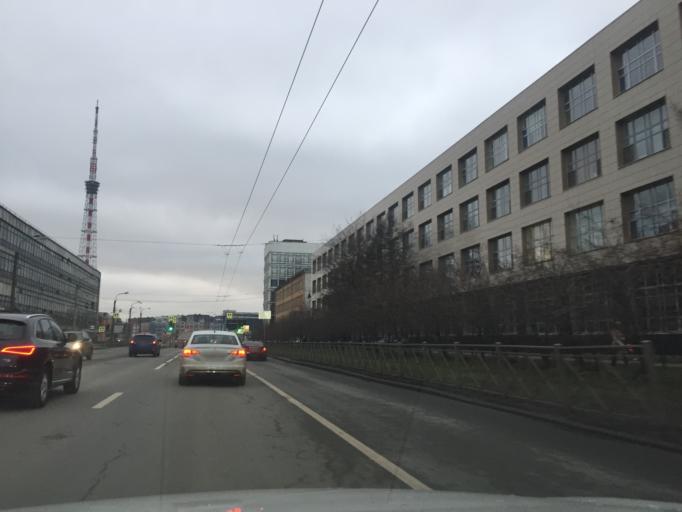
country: RU
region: Leningrad
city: Sampsonievskiy
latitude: 59.9823
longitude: 30.3297
